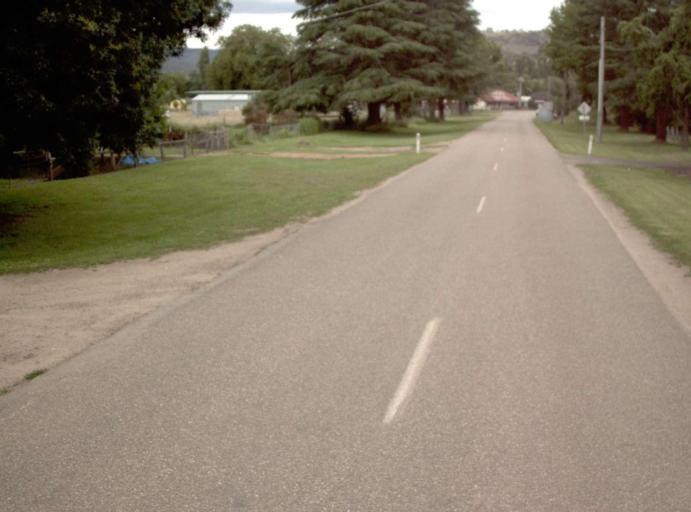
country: AU
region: Victoria
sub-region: East Gippsland
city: Bairnsdale
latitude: -37.4597
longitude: 147.2507
